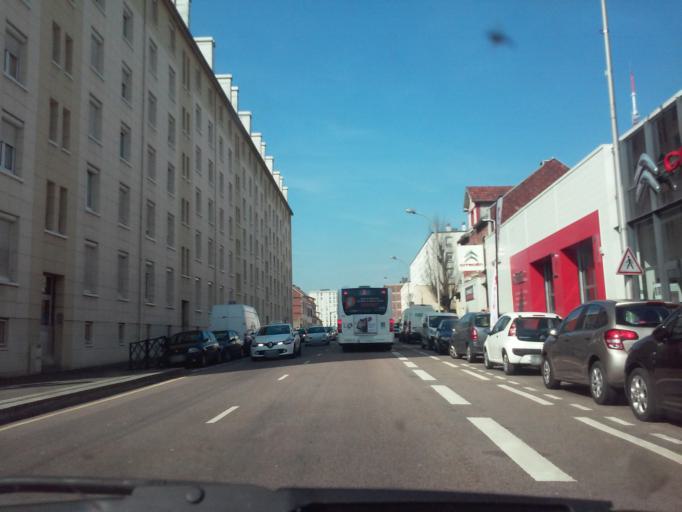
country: FR
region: Haute-Normandie
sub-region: Departement de la Seine-Maritime
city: Harfleur
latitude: 49.5024
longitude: 0.1817
